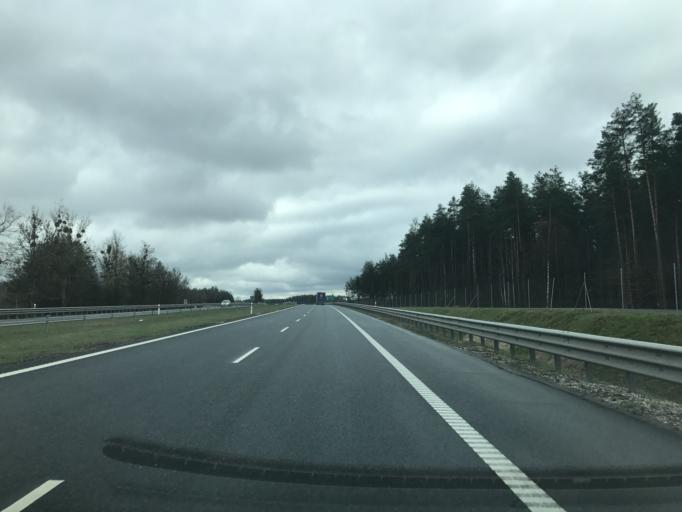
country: PL
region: Warmian-Masurian Voivodeship
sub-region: Powiat olsztynski
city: Olsztynek
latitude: 53.5420
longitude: 20.2717
